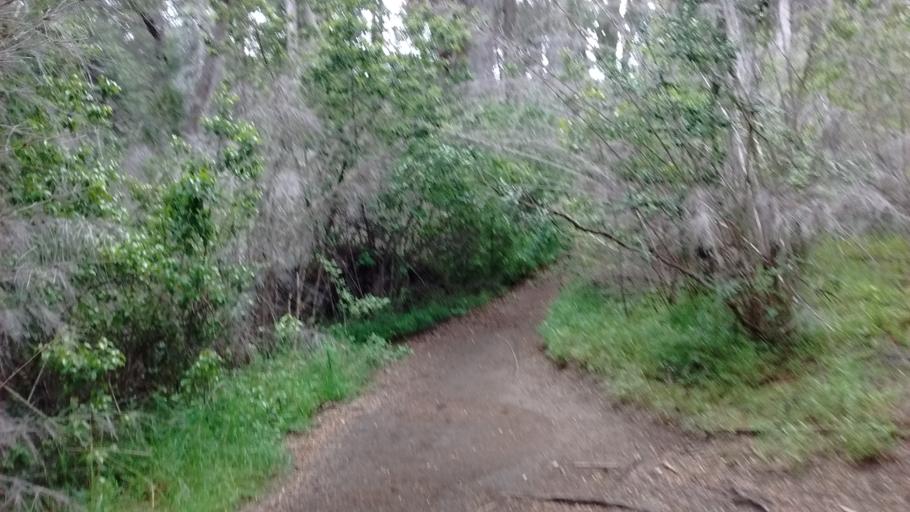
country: AR
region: Rio Negro
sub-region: Departamento de Bariloche
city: San Carlos de Bariloche
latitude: -41.0589
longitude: -71.5655
